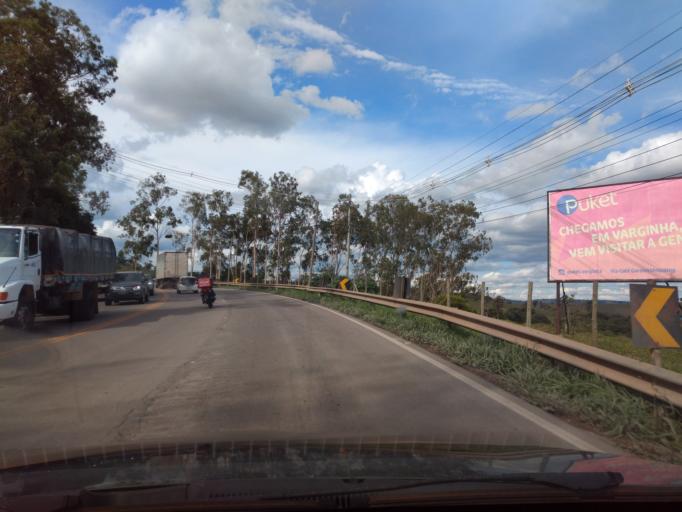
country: BR
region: Minas Gerais
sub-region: Varginha
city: Varginha
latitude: -21.6068
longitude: -45.4319
